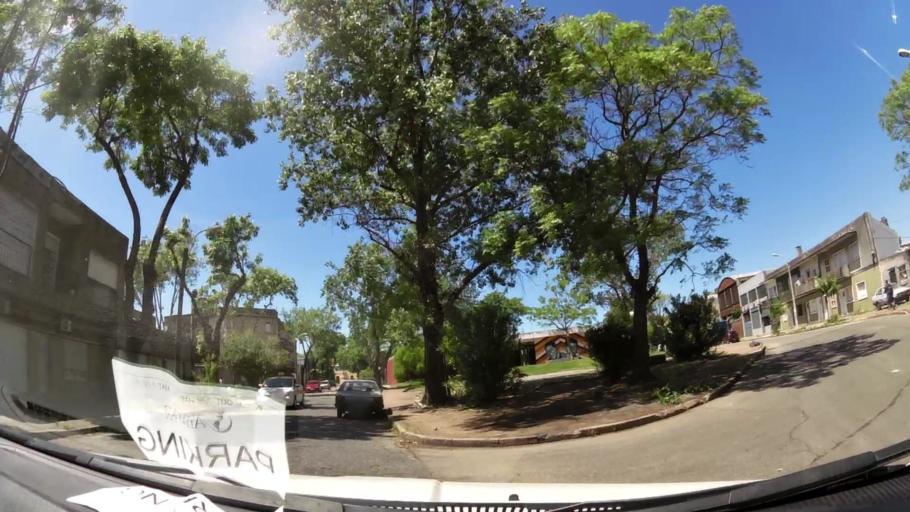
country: UY
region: Montevideo
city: Montevideo
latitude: -34.8767
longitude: -56.1734
